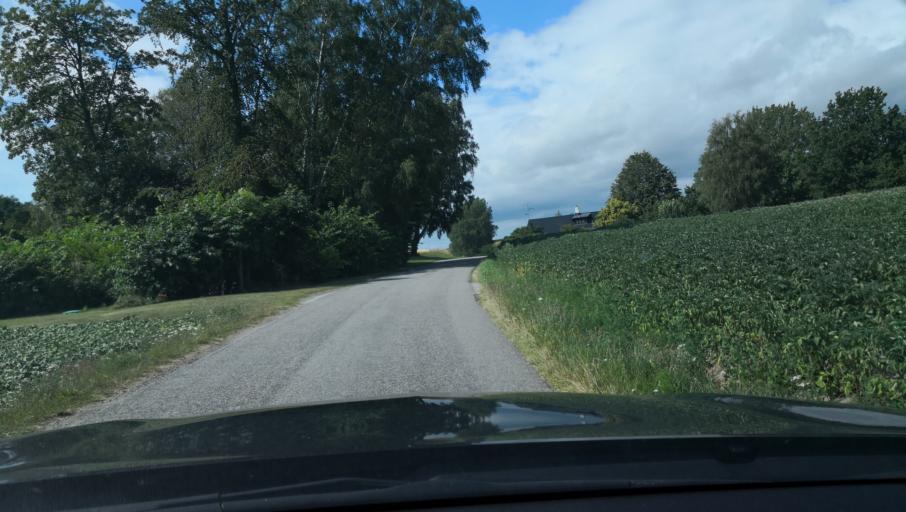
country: SE
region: Skane
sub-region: Ystads Kommun
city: Kopingebro
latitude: 55.3888
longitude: 14.1425
